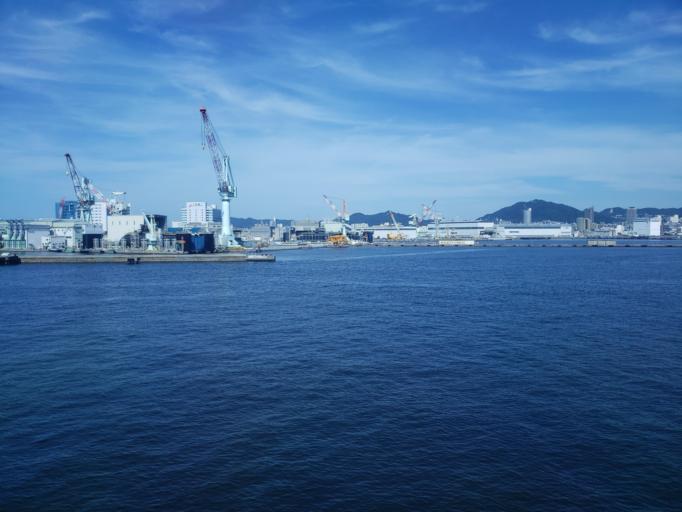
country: JP
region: Hyogo
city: Kobe
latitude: 34.6563
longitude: 135.1888
